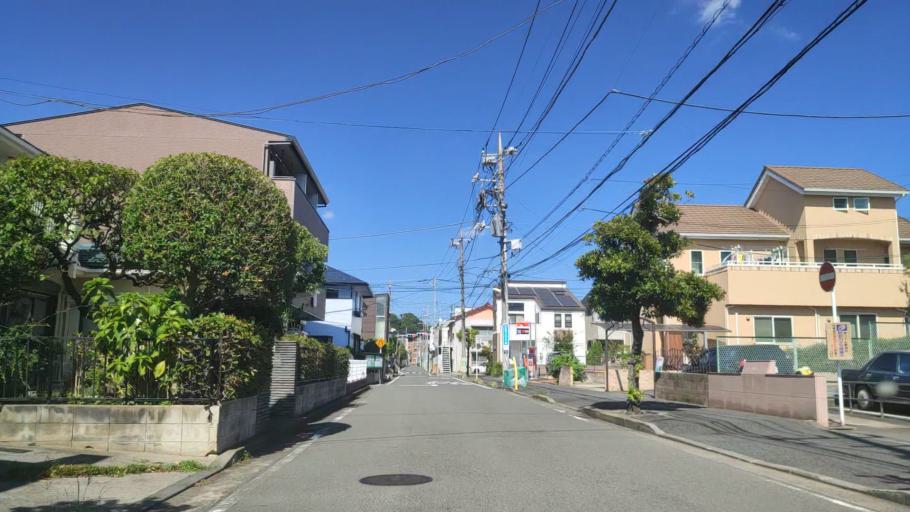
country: JP
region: Kanagawa
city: Yokohama
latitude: 35.5196
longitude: 139.6244
